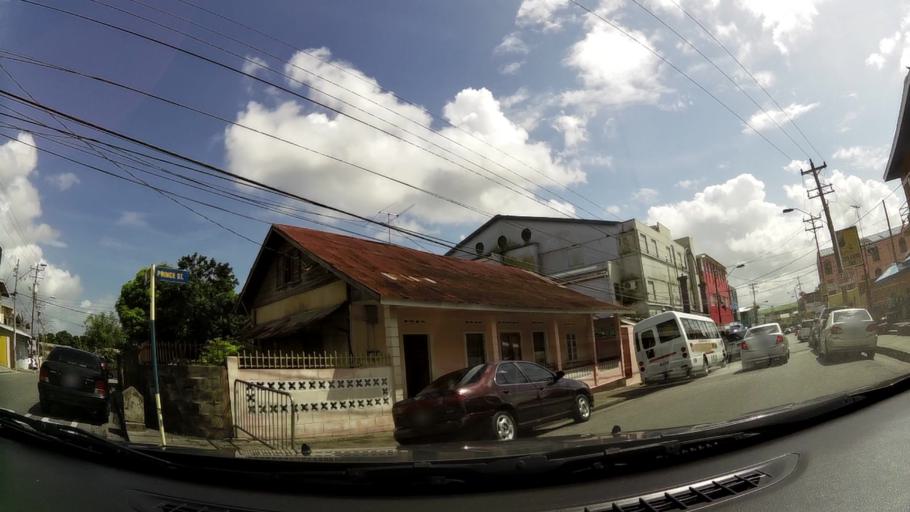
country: TT
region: Borough of Arima
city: Arima
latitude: 10.6425
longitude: -61.2807
